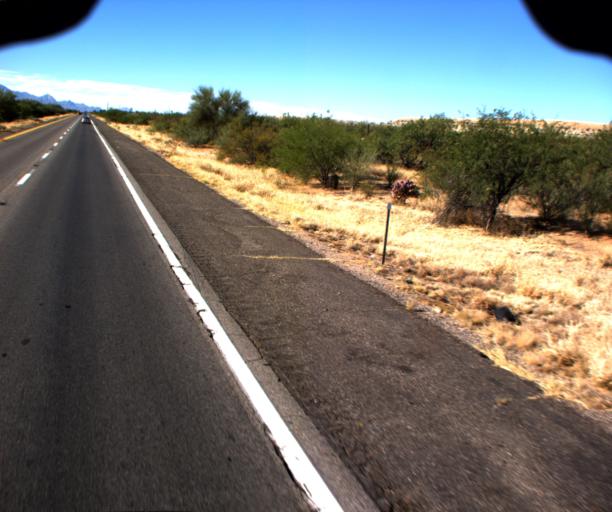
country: US
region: Arizona
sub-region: Pima County
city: Sahuarita
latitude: 31.9823
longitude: -110.9912
